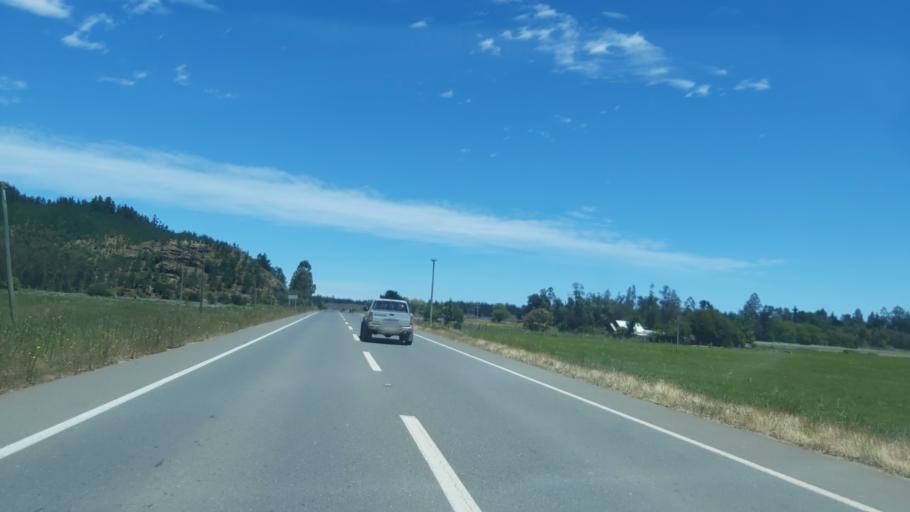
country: CL
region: Maule
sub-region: Provincia de Talca
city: Constitucion
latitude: -35.2786
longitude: -72.3533
